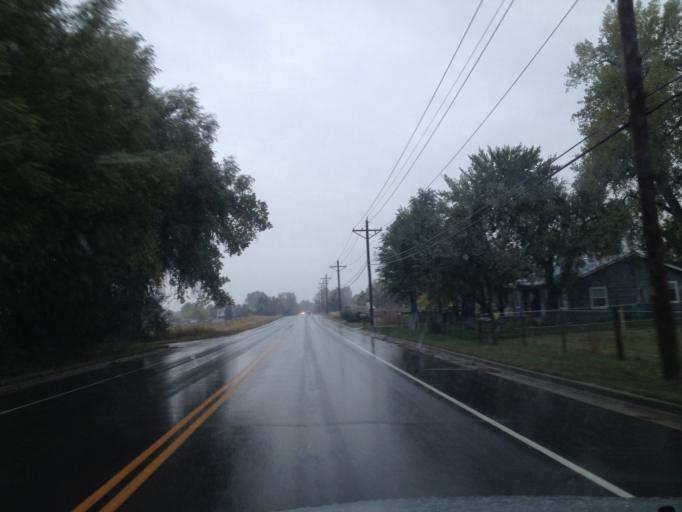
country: US
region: Colorado
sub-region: Boulder County
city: Superior
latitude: 39.9935
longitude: -105.1752
